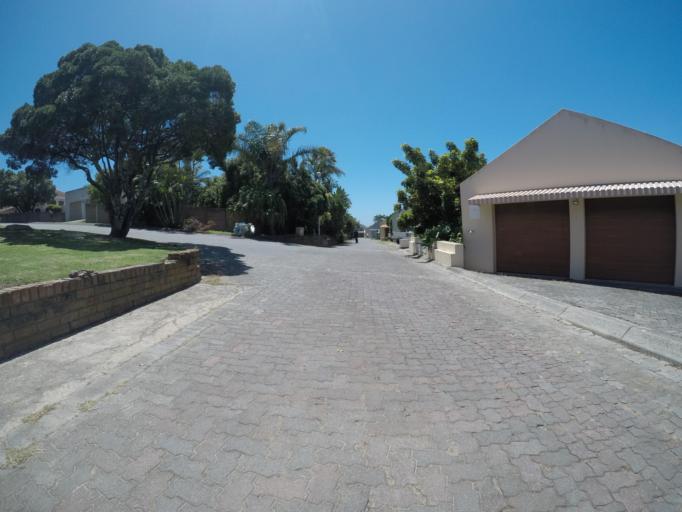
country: ZA
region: Eastern Cape
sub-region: Buffalo City Metropolitan Municipality
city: East London
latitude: -32.9672
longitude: 27.9545
